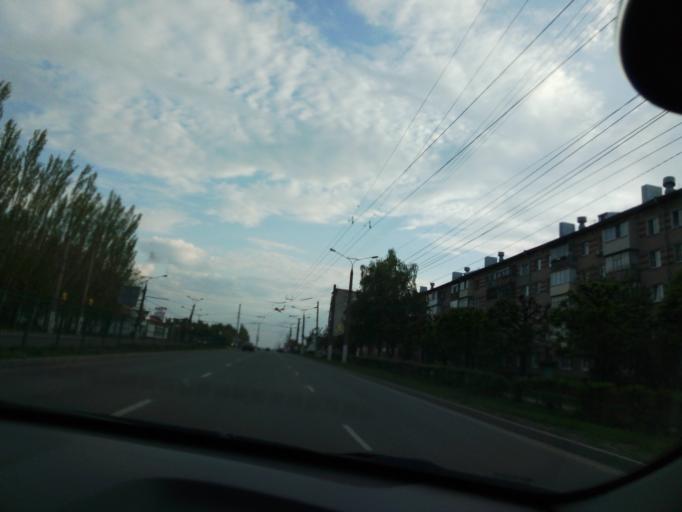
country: RU
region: Chuvashia
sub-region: Cheboksarskiy Rayon
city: Cheboksary
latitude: 56.1269
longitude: 47.2849
